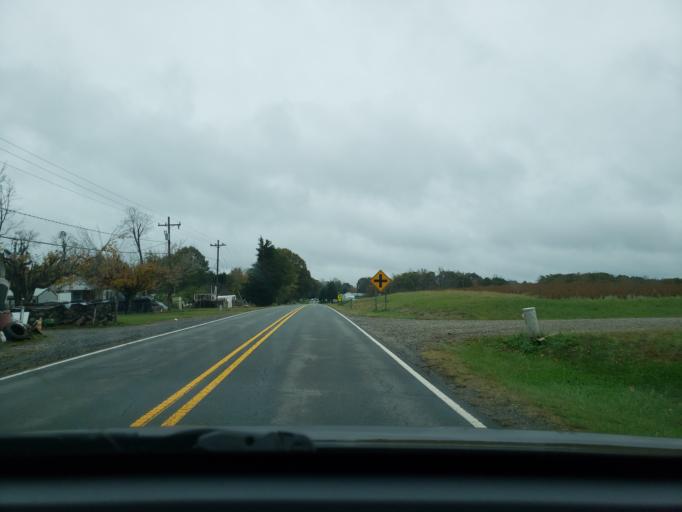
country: US
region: North Carolina
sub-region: Stokes County
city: Walnut Cove
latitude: 36.3288
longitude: -80.1463
